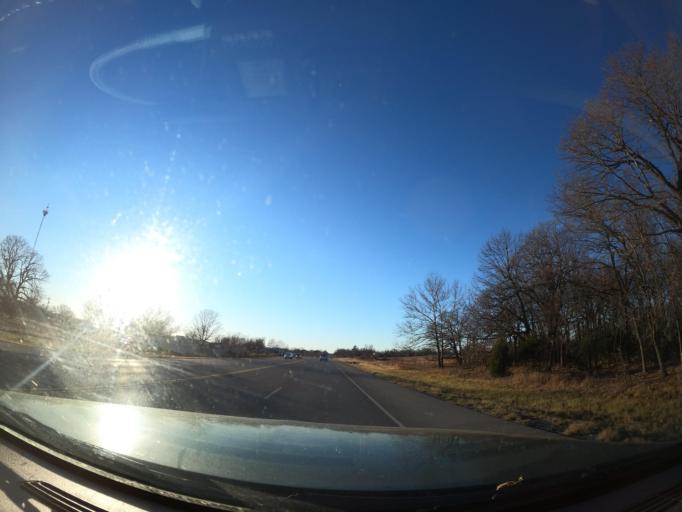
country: US
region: Oklahoma
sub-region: Pittsburg County
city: Krebs
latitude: 34.8941
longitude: -95.6345
